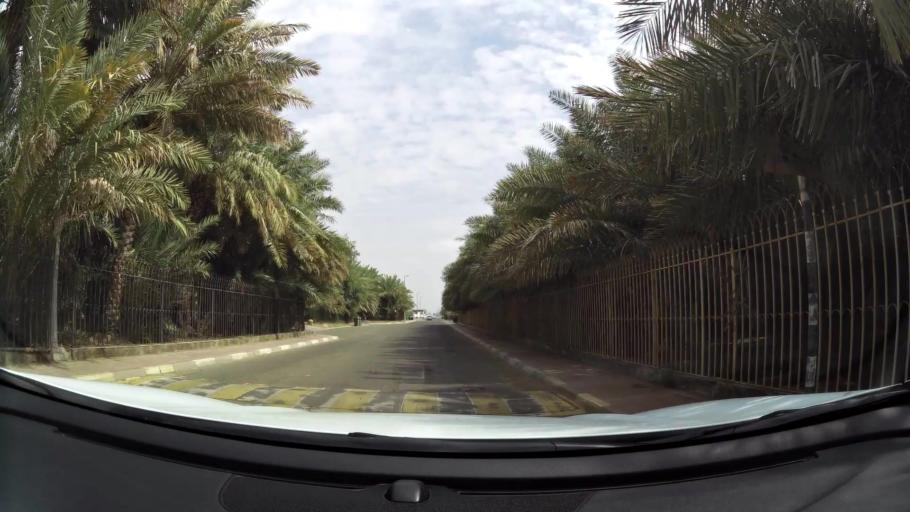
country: AE
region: Abu Dhabi
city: Al Ain
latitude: 24.1994
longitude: 55.7987
